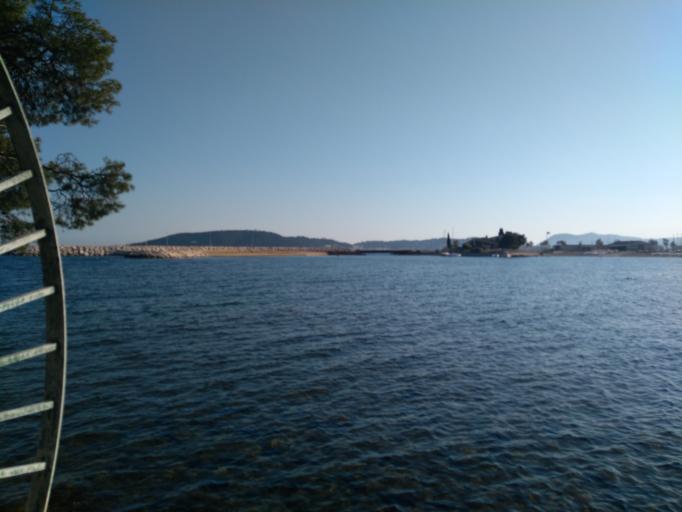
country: FR
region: Provence-Alpes-Cote d'Azur
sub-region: Departement du Var
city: Toulon
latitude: 43.1084
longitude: 5.9567
